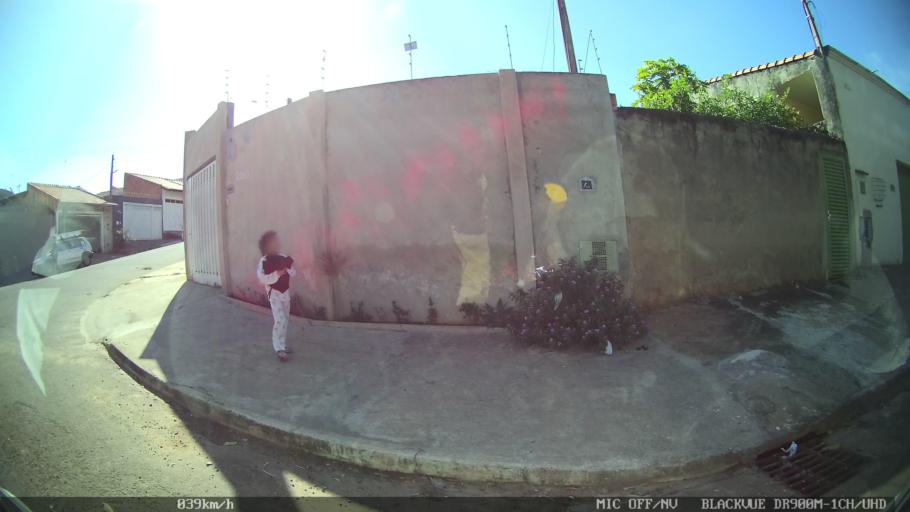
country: BR
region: Sao Paulo
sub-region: Franca
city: Franca
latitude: -20.4908
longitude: -47.4225
